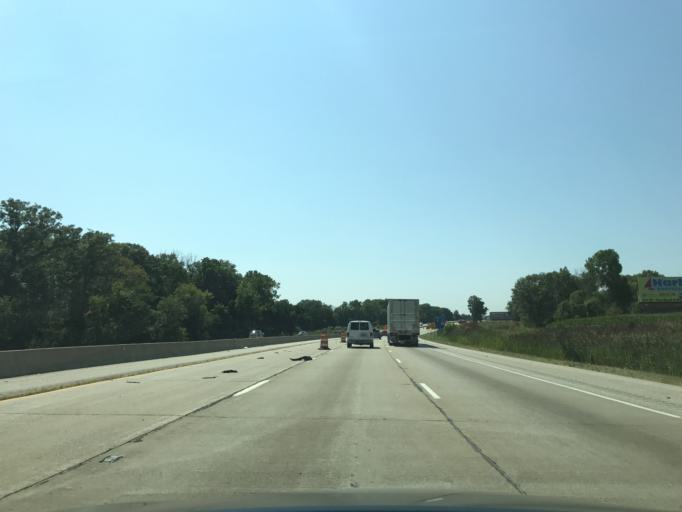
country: US
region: Indiana
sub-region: Porter County
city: Chesterton
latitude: 41.6271
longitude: -87.0228
